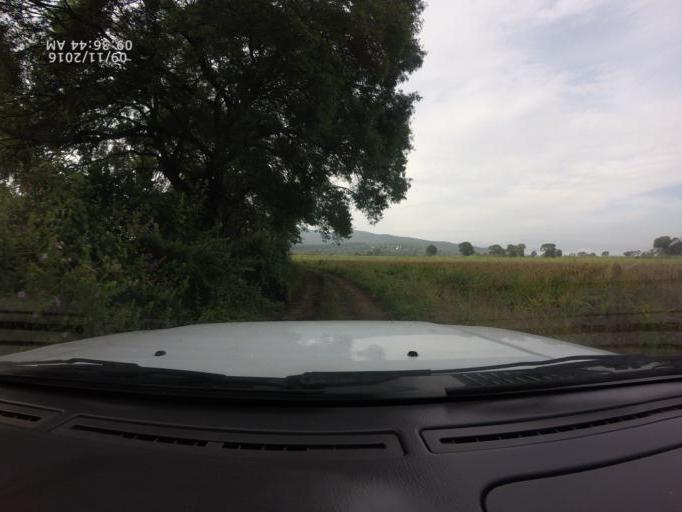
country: MX
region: Michoacan
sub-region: Morelia
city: La Mintzita (Piedra Dura)
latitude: 19.5701
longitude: -101.2904
